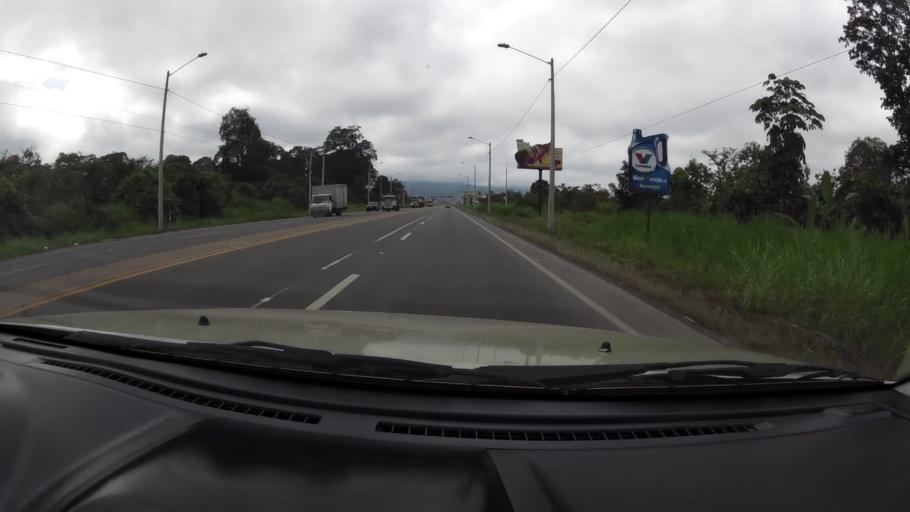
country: EC
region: Guayas
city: Naranjal
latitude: -2.6578
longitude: -79.6162
